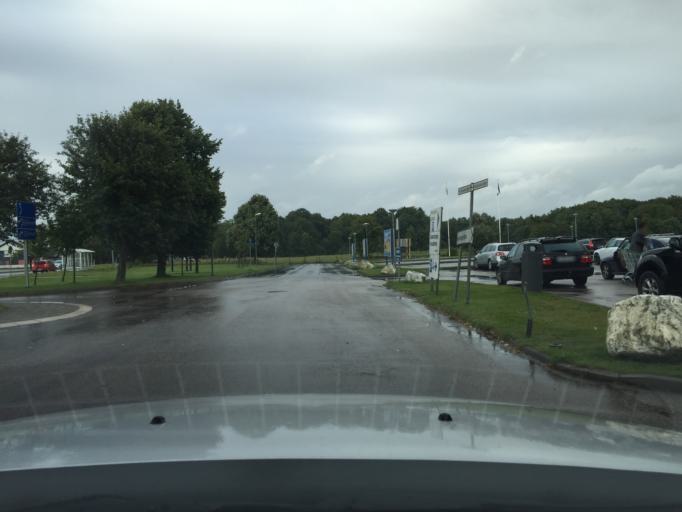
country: SE
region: Skane
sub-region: Hoors Kommun
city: Hoeoer
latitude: 55.9515
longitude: 13.5622
